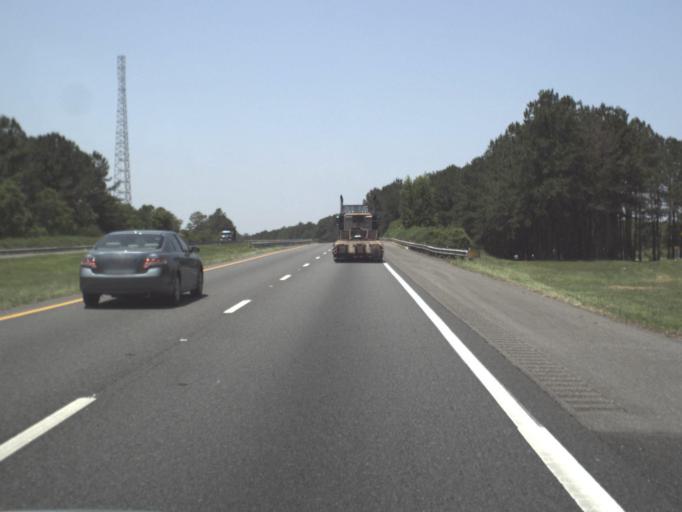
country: US
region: Florida
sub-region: Baker County
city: Macclenny
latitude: 30.2616
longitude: -82.1600
